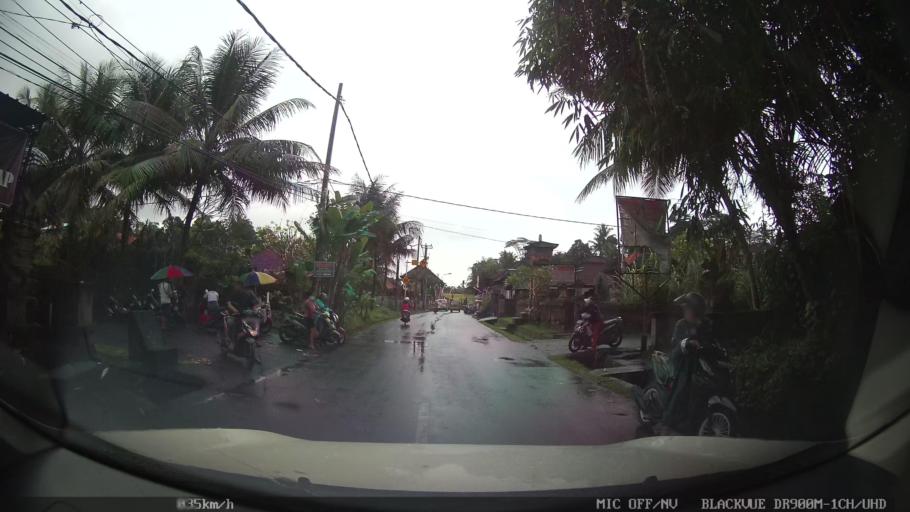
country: ID
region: Bali
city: Banjar Teguan
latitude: -8.5050
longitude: 115.2299
